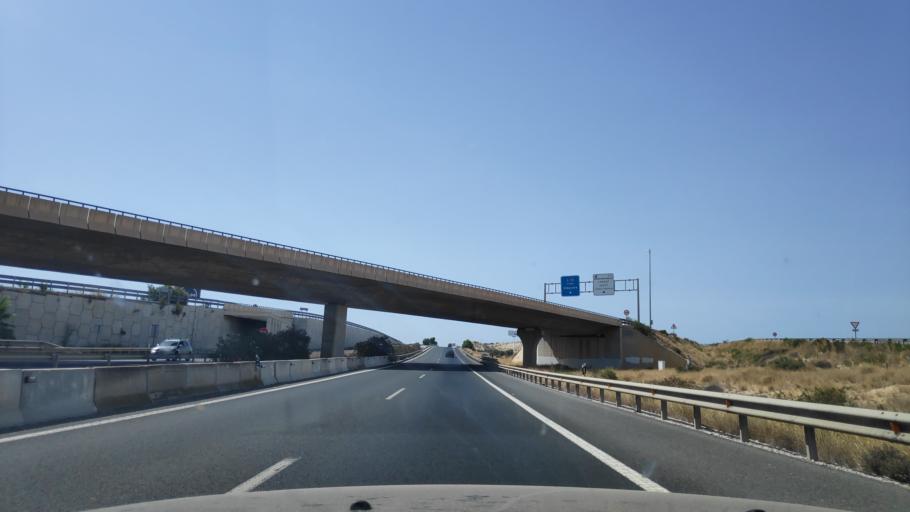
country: ES
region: Murcia
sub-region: Murcia
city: Lorqui
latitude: 38.0995
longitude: -1.2312
